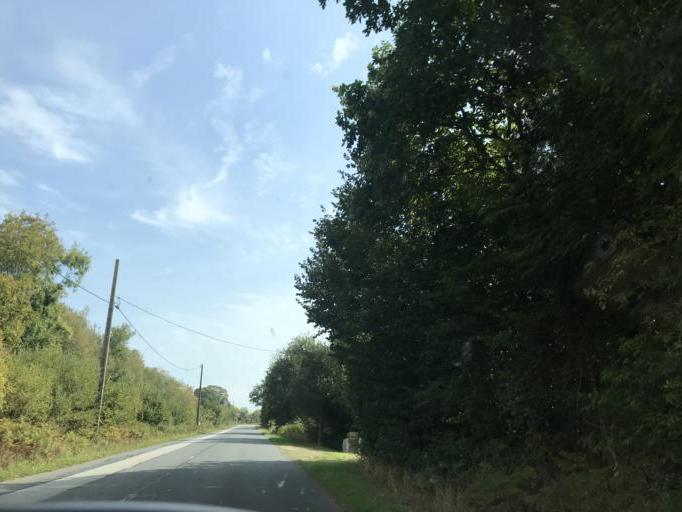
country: FR
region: Brittany
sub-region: Departement du Finistere
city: Le Faou
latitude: 48.2905
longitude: -4.1675
